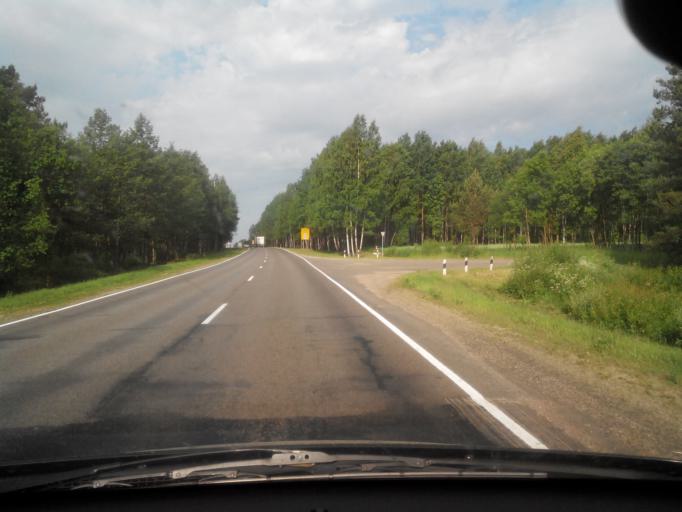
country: BY
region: Minsk
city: Myadzyel
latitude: 55.0616
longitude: 27.1508
